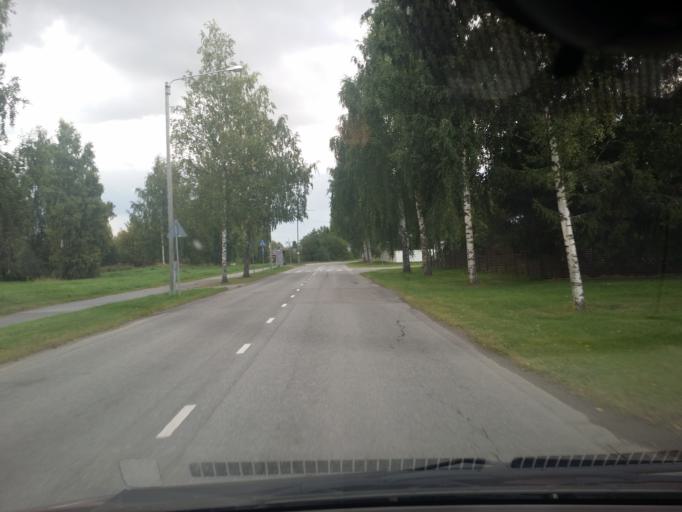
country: FI
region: Satakunta
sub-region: Pori
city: Pori
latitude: 61.5050
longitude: 21.8108
